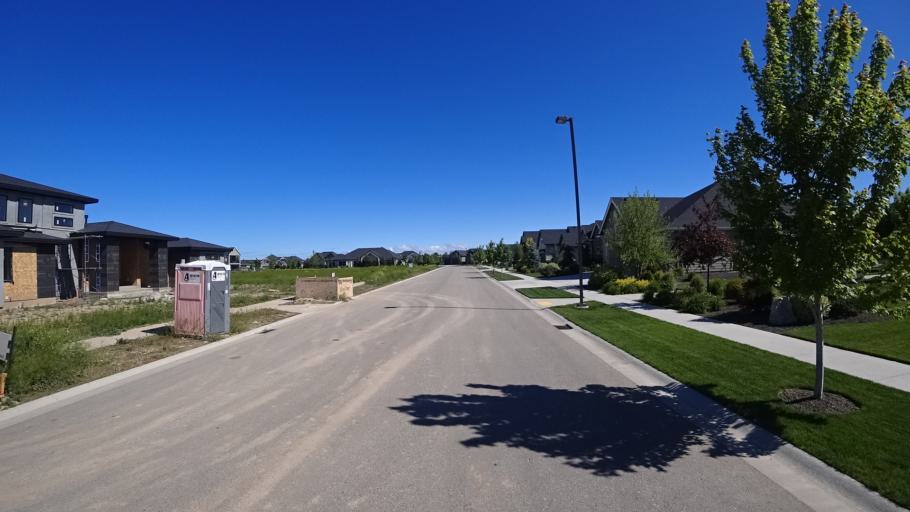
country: US
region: Idaho
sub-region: Ada County
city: Eagle
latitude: 43.6655
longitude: -116.3978
